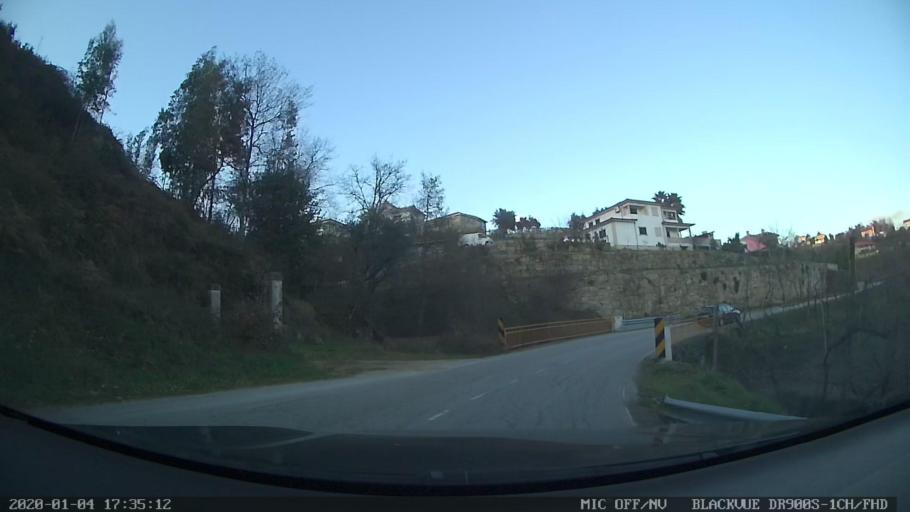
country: PT
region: Vila Real
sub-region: Mondim de Basto
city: Mondim de Basto
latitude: 41.4427
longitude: -7.9719
